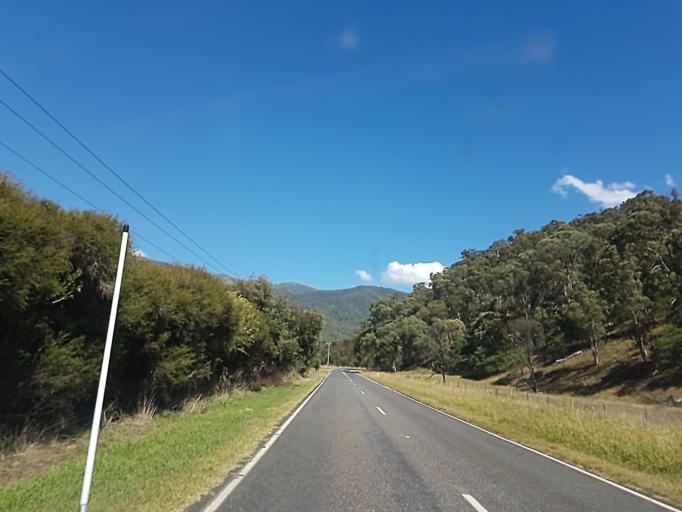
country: AU
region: Victoria
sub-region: Alpine
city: Mount Beauty
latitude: -36.8377
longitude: 147.0774
